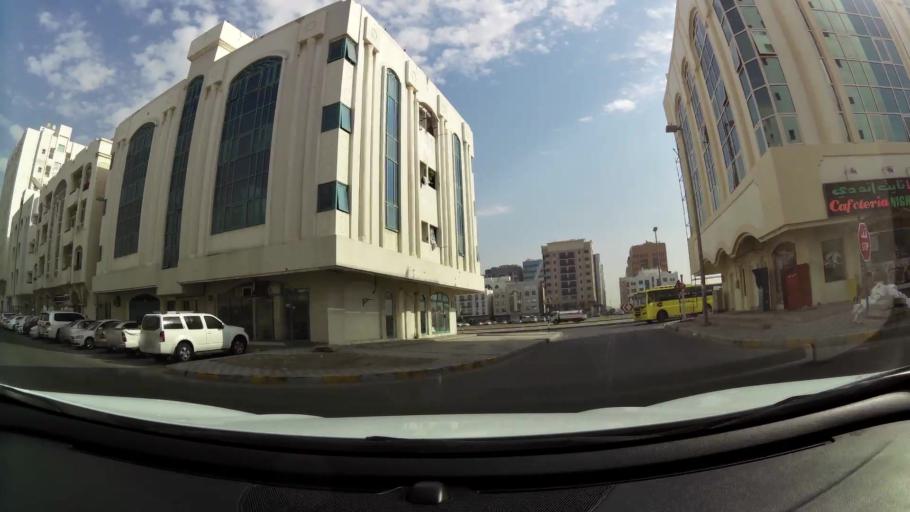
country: AE
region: Abu Dhabi
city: Abu Dhabi
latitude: 24.3223
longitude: 54.5359
